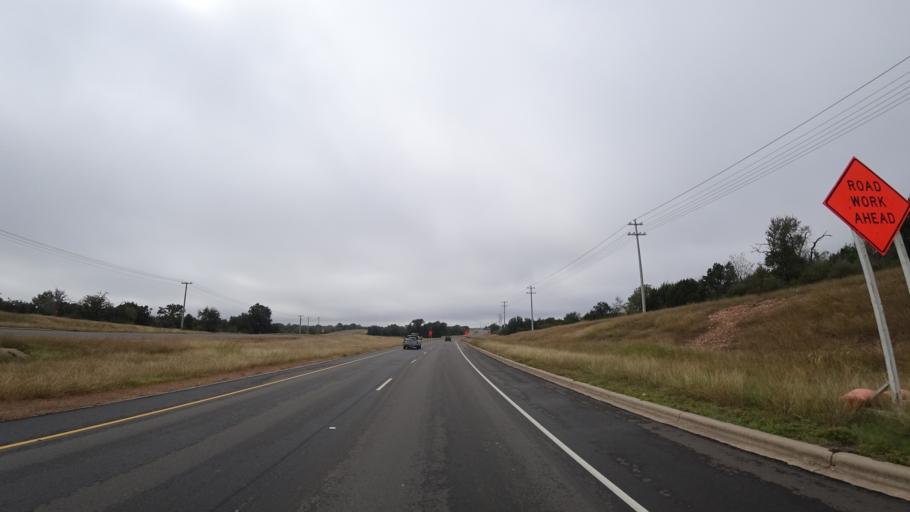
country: US
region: Texas
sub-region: Travis County
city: Shady Hollow
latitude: 30.1850
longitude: -97.8791
